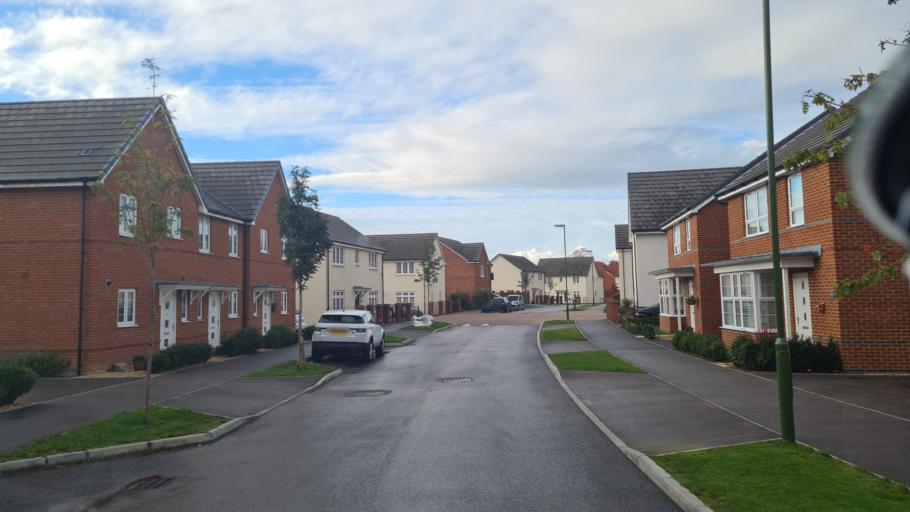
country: GB
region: England
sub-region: West Sussex
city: Littlehampton
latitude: 50.8243
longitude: -0.5589
